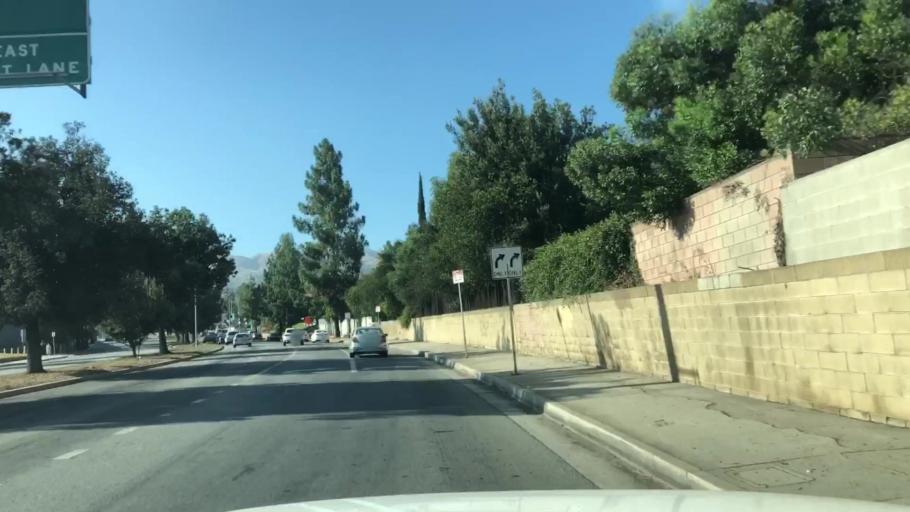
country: US
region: California
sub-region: Los Angeles County
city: Northridge
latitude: 34.2699
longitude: -118.5551
